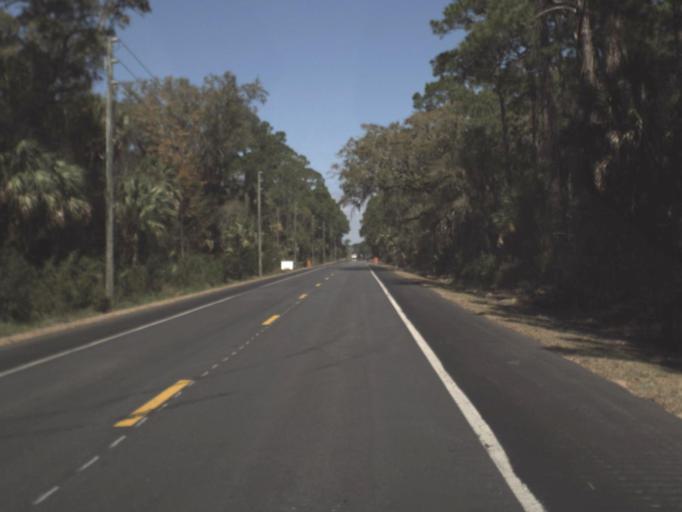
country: US
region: Florida
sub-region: Gulf County
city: Port Saint Joe
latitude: 29.7273
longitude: -85.3028
